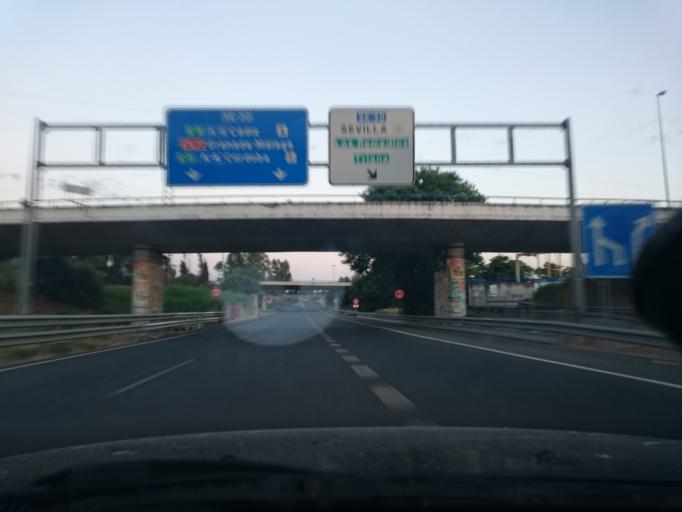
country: ES
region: Andalusia
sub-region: Provincia de Sevilla
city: San Juan de Aznalfarache
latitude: 37.3730
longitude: -6.0156
